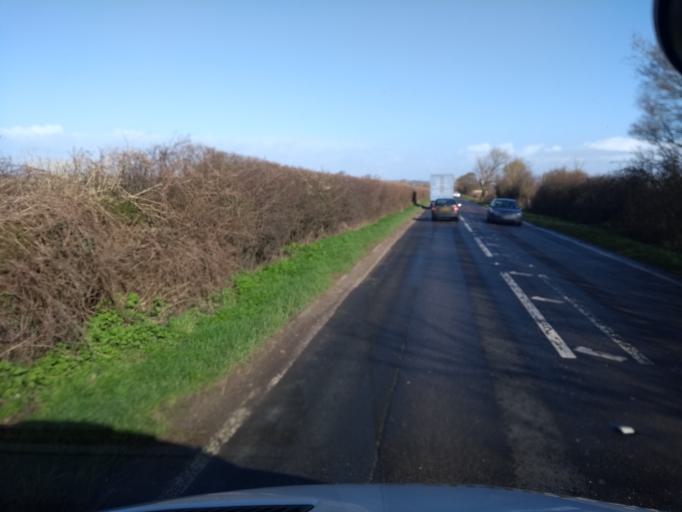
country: GB
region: England
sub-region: Somerset
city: Ilchester
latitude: 50.9868
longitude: -2.6768
